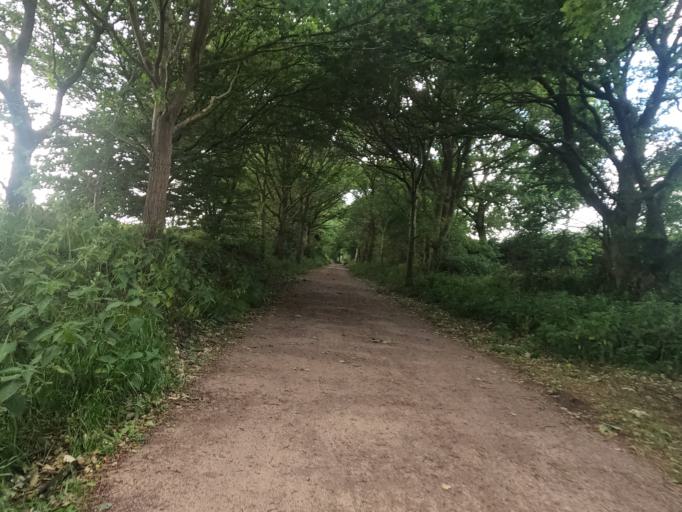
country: GB
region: England
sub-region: Cheshire West and Chester
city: Over
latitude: 53.2049
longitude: -2.5682
